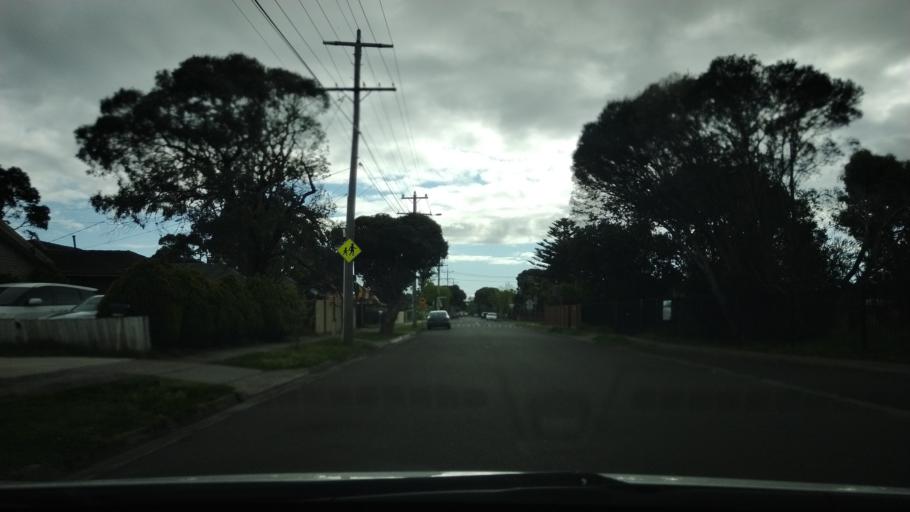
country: AU
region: Victoria
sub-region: Greater Dandenong
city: Springvale South
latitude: -37.9828
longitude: 145.1515
